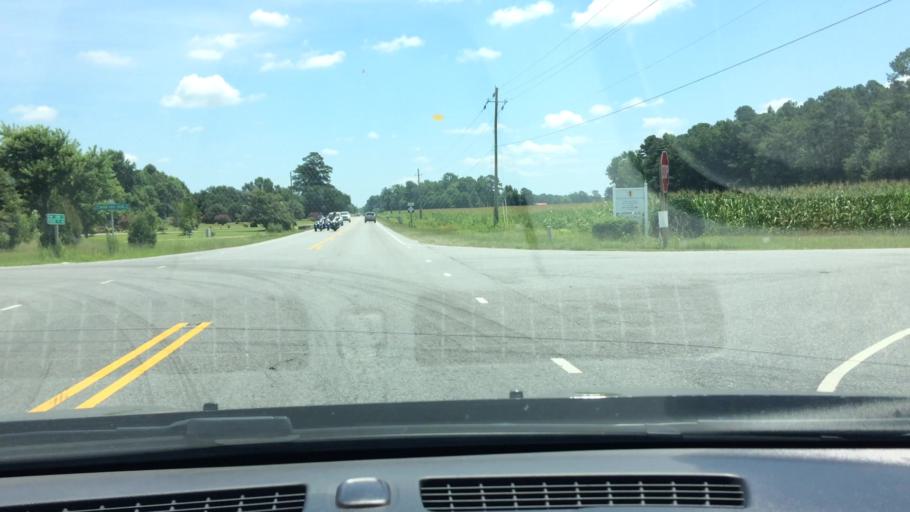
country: US
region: North Carolina
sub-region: Pitt County
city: Ayden
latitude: 35.4712
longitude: -77.3851
